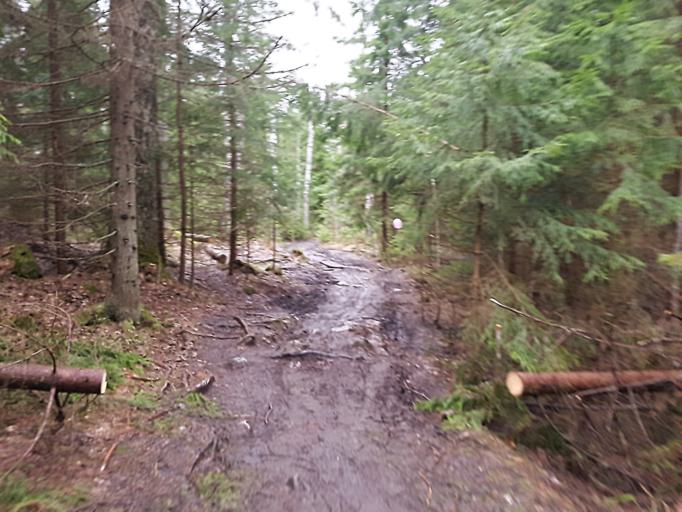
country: FI
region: Uusimaa
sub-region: Helsinki
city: Helsinki
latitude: 60.2622
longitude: 24.9212
